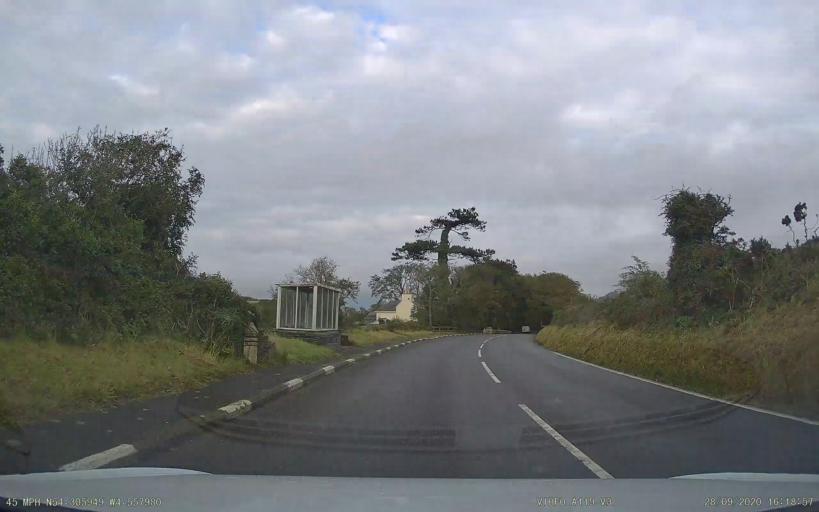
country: IM
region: Douglas
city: Douglas
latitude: 54.3060
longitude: -4.5580
